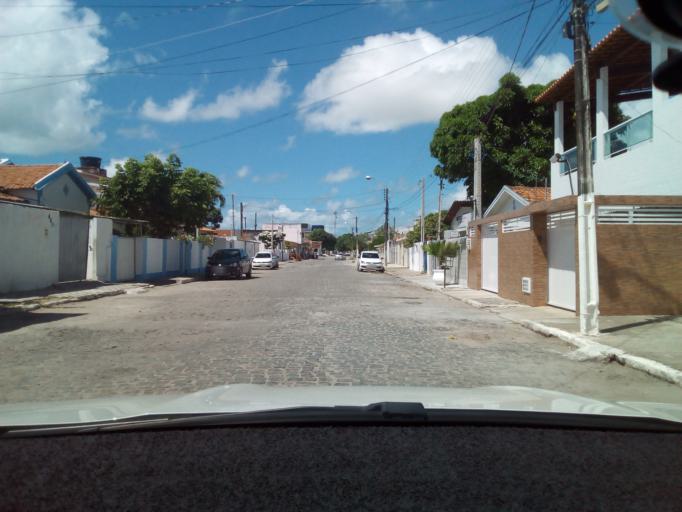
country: BR
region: Paraiba
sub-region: Cabedelo
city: Cabedelo
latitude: -6.9791
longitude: -34.8340
